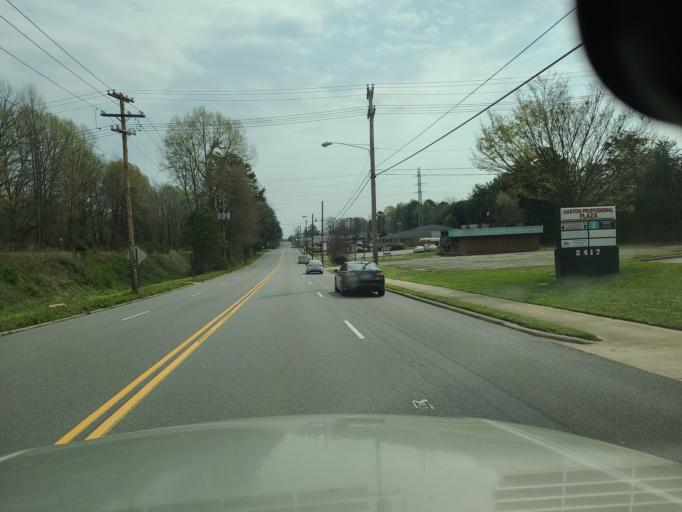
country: US
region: North Carolina
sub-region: Gaston County
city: Ranlo
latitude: 35.2799
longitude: -81.1440
